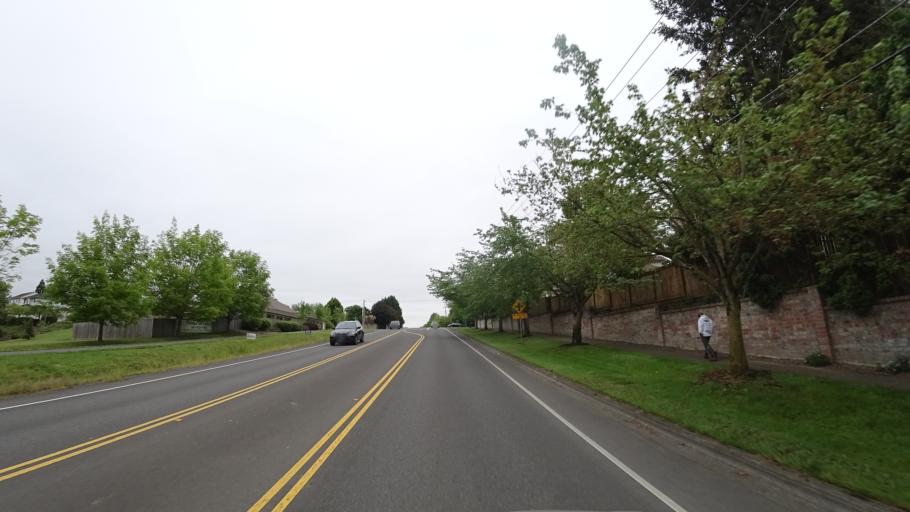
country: US
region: Oregon
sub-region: Washington County
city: Bethany
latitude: 45.5555
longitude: -122.8587
